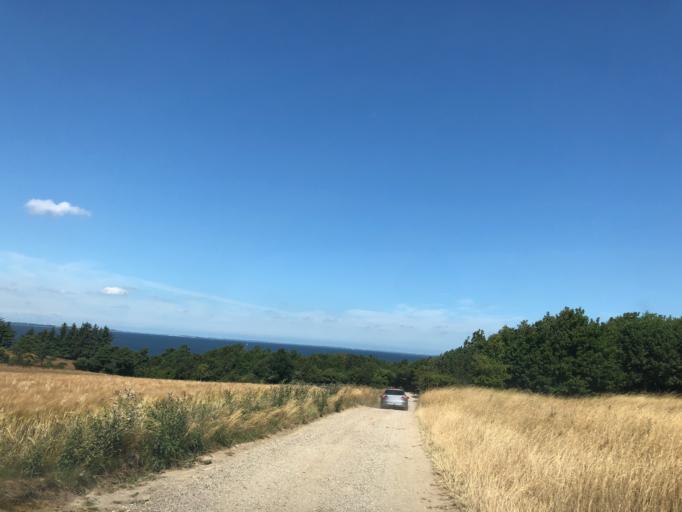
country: DK
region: North Denmark
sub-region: Morso Kommune
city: Nykobing Mors
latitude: 56.8390
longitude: 9.0041
